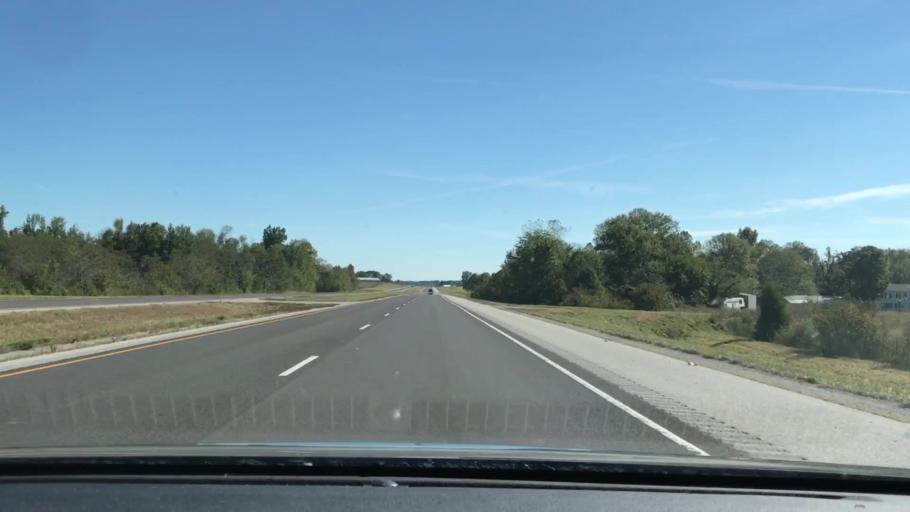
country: US
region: Kentucky
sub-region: Todd County
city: Elkton
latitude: 36.8036
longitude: -87.0784
